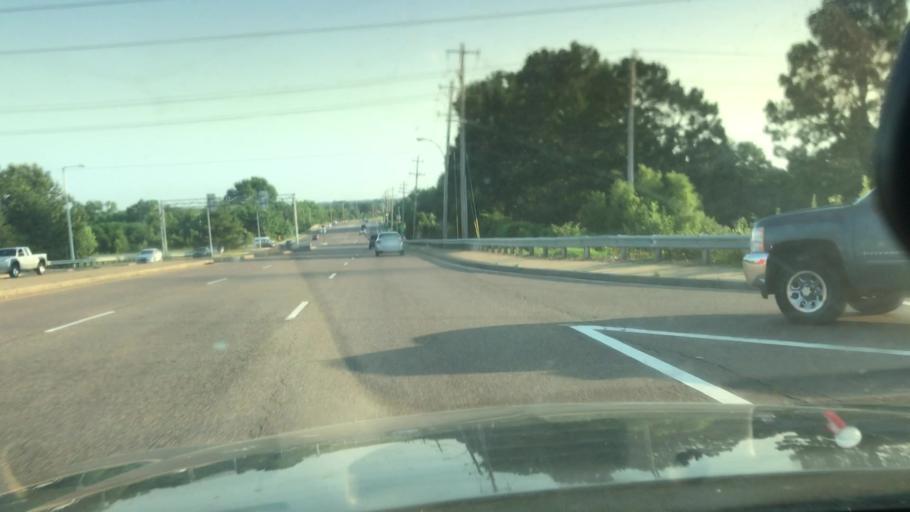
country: US
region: Tennessee
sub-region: Shelby County
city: Bartlett
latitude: 35.1868
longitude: -89.8135
